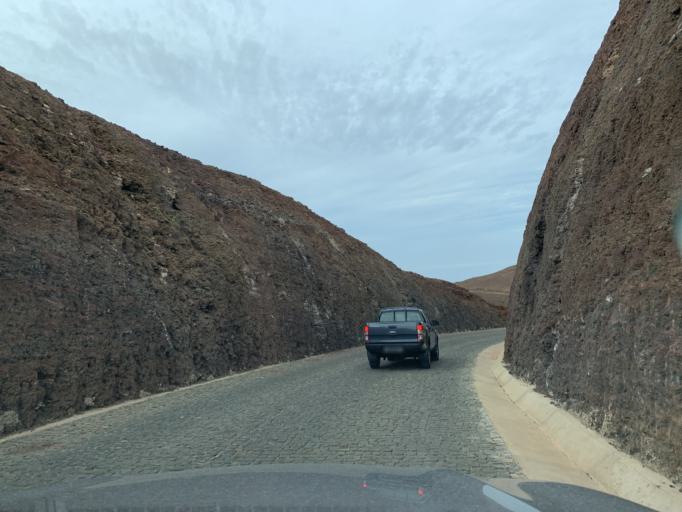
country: CV
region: Porto Novo
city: Porto Novo
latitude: 16.9657
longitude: -25.2745
